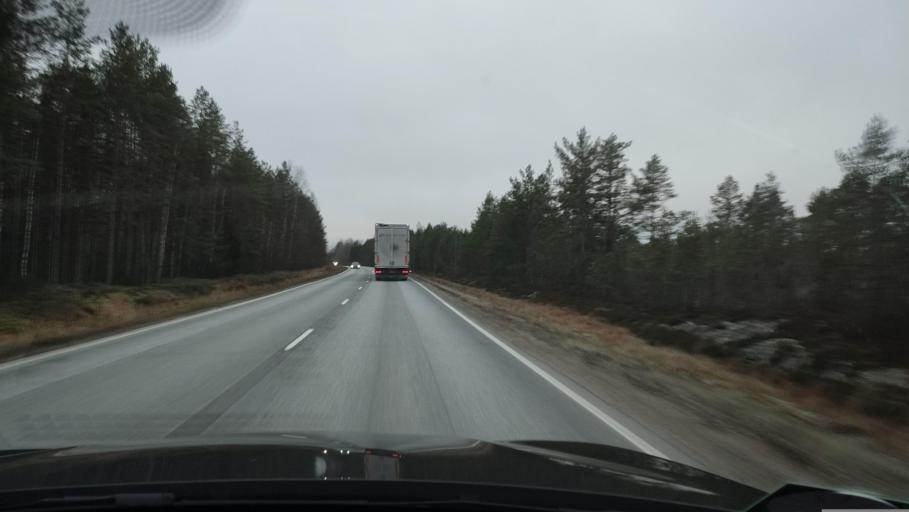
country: FI
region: Southern Ostrobothnia
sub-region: Suupohja
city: Kauhajoki
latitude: 62.3813
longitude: 22.1104
